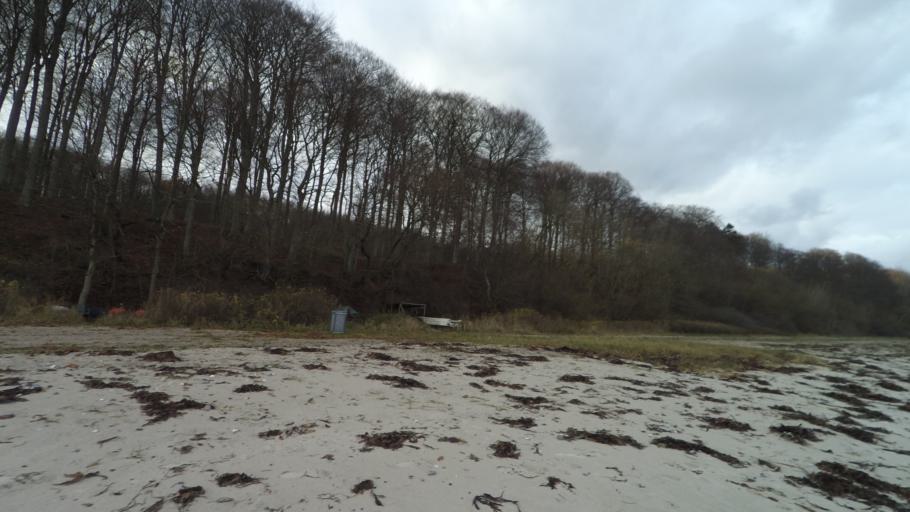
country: DK
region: Central Jutland
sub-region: Arhus Kommune
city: Beder
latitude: 56.0650
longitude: 10.2585
